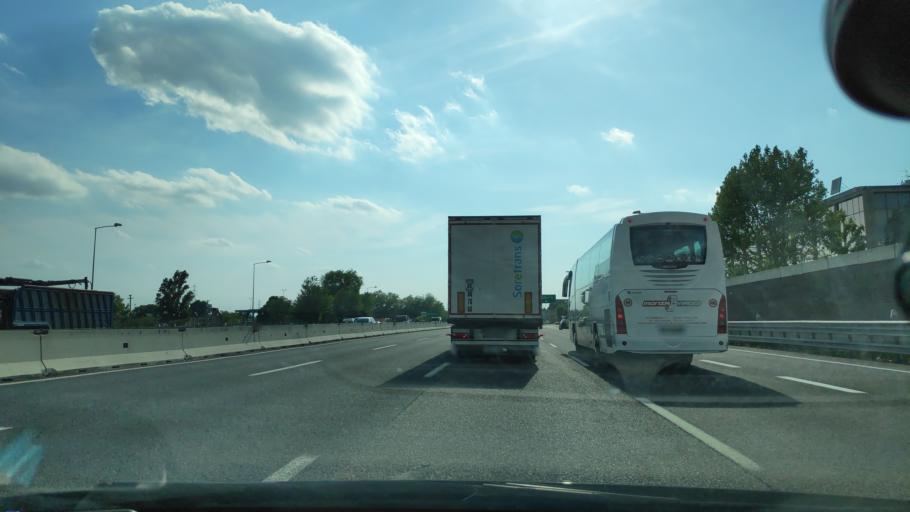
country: IT
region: Lombardy
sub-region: Provincia di Monza e Brianza
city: Caponago
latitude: 45.5707
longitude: 9.3651
